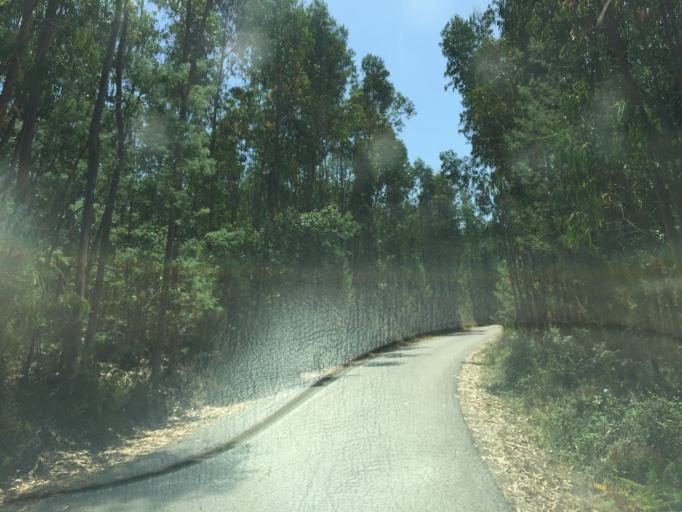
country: PT
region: Santarem
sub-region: Ferreira do Zezere
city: Ferreira do Zezere
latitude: 39.6466
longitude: -8.2991
